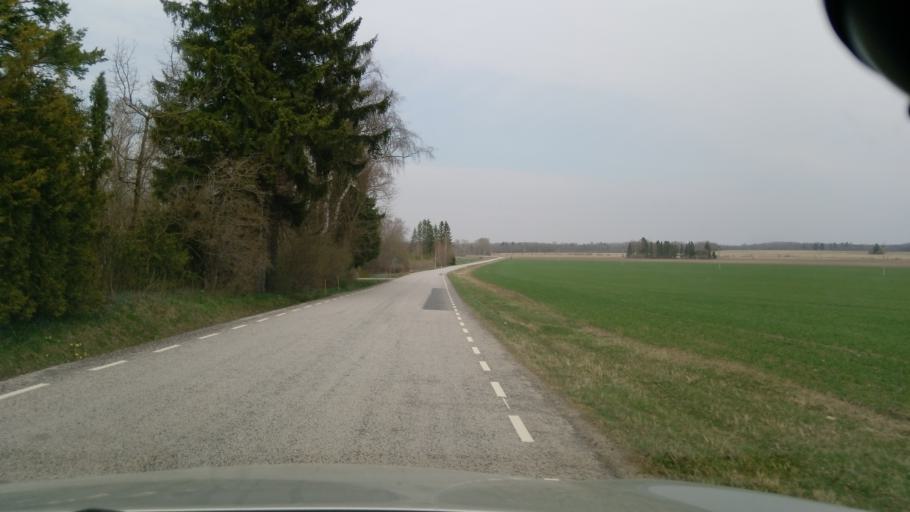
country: EE
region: Jaervamaa
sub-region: Tueri vald
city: Sarevere
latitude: 58.7868
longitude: 25.4739
